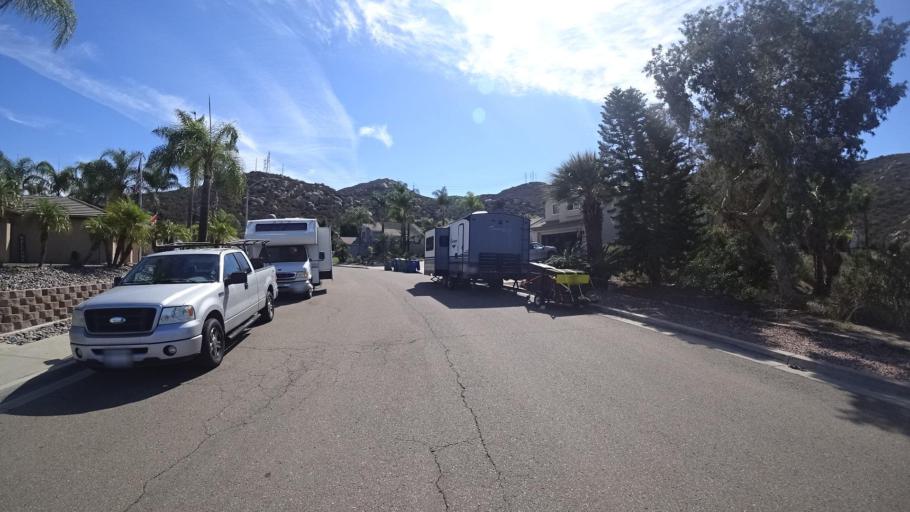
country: US
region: California
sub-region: San Diego County
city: Granite Hills
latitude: 32.8285
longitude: -116.8937
